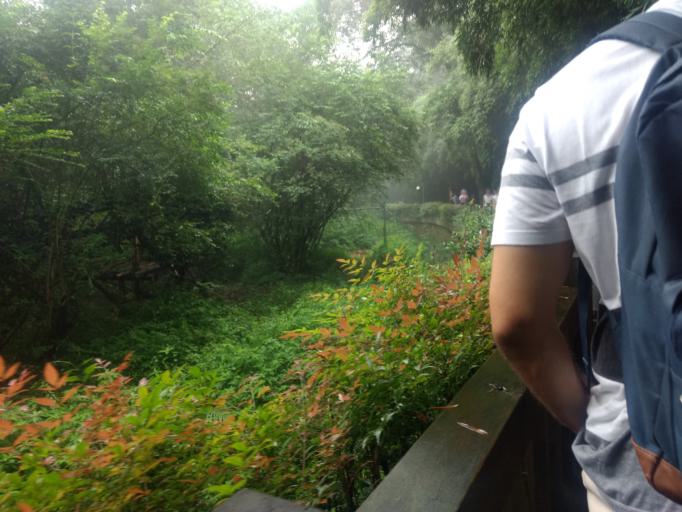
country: CN
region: Sichuan
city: Xindu
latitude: 30.7380
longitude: 104.1411
